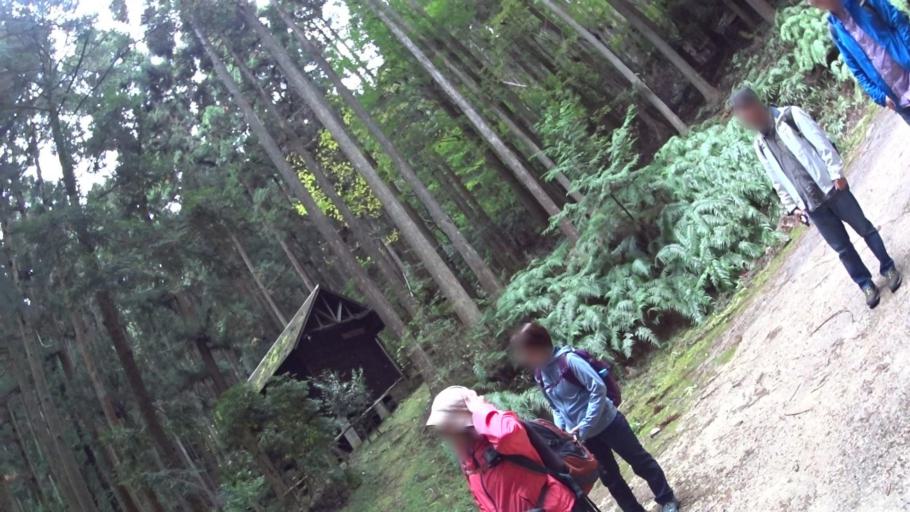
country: JP
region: Kyoto
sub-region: Kyoto-shi
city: Kamigyo-ku
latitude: 35.1105
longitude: 135.7813
